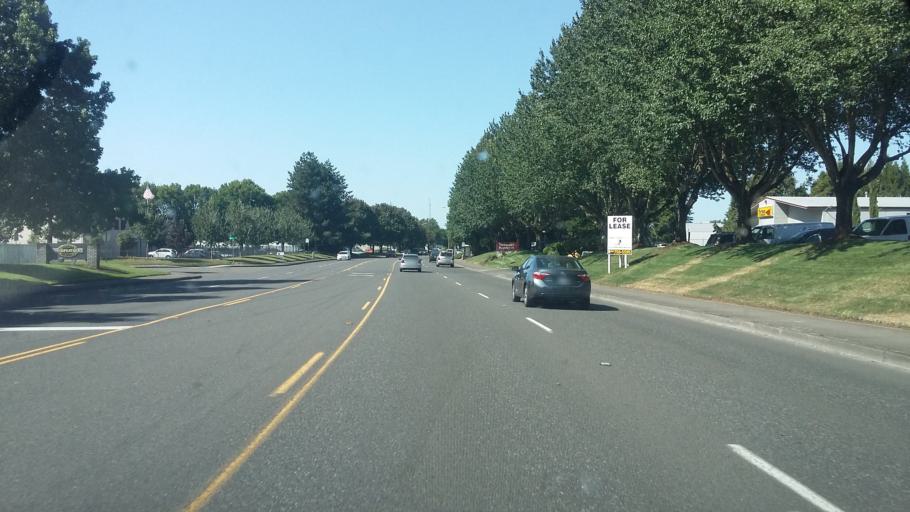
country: US
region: Washington
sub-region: Clark County
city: Orchards
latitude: 45.6459
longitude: -122.5580
